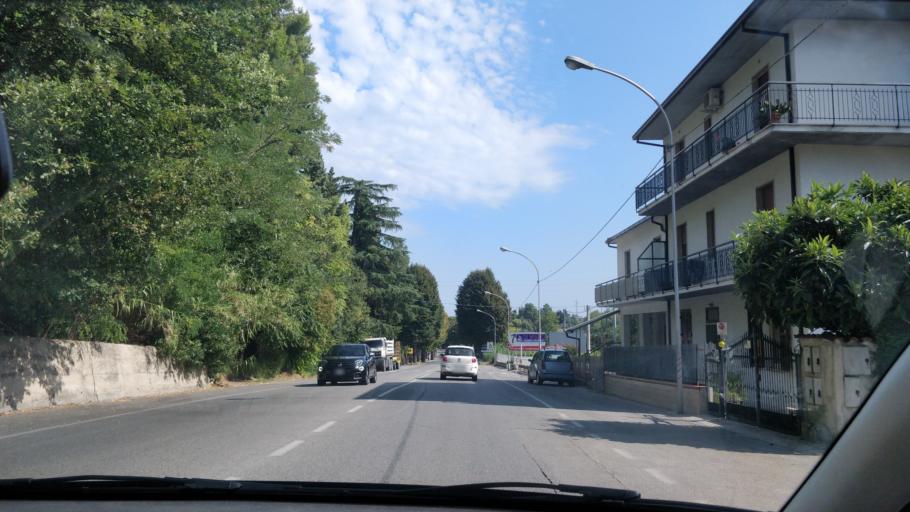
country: IT
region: Abruzzo
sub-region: Provincia di Chieti
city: Chieti
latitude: 42.3881
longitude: 14.1570
